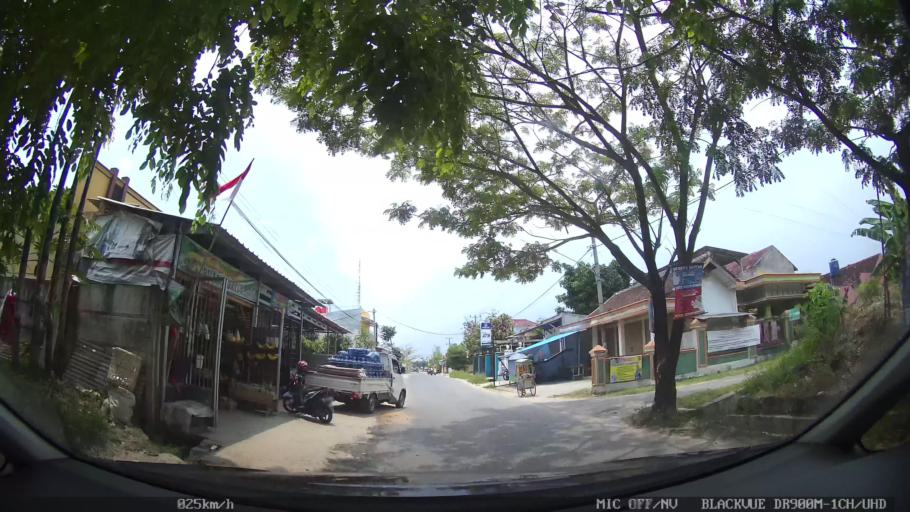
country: ID
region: Lampung
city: Kedaton
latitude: -5.3944
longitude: 105.3054
